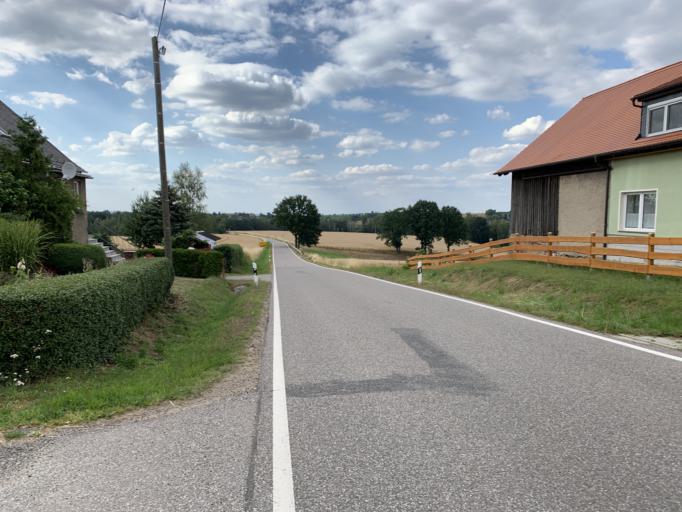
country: DE
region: Saxony
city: Seelitz
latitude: 51.0207
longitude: 12.8276
